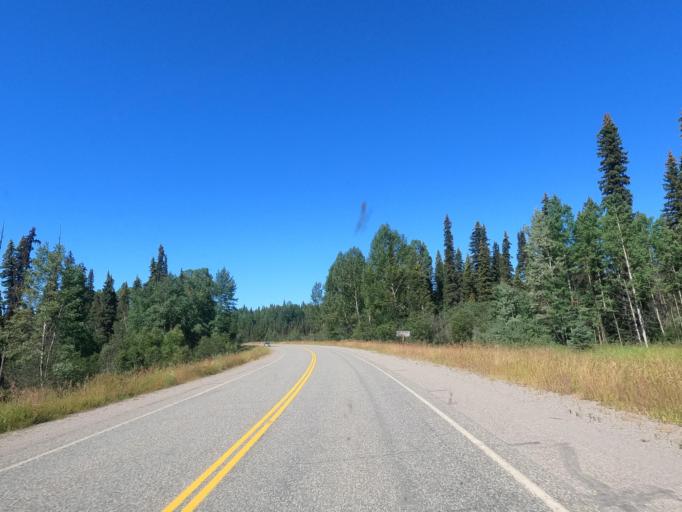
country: CA
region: British Columbia
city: Quesnel
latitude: 53.0557
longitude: -122.1694
